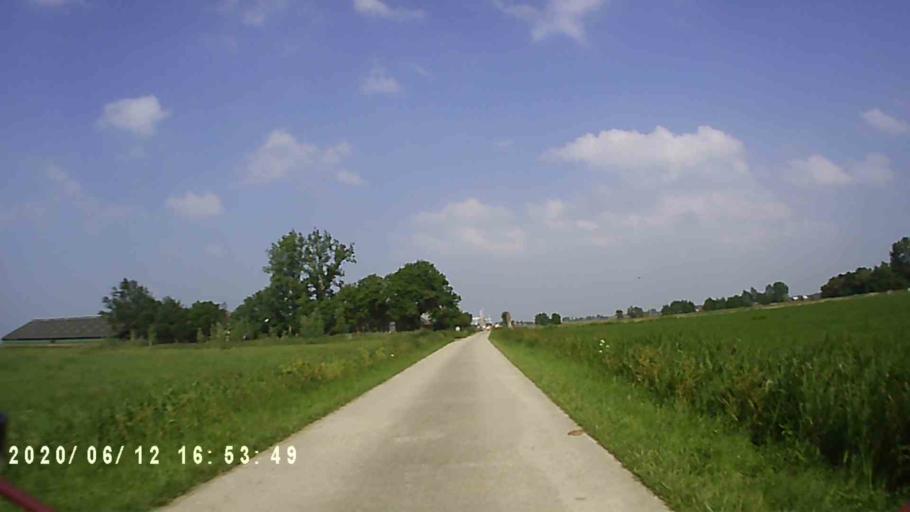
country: NL
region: Groningen
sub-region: Gemeente Groningen
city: Korrewegwijk
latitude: 53.2638
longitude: 6.5421
